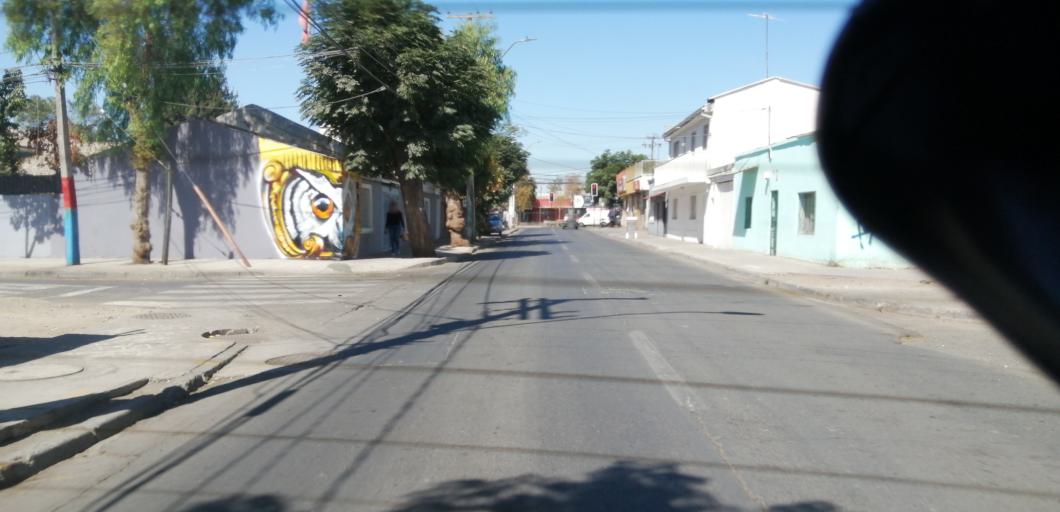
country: CL
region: Santiago Metropolitan
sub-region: Provincia de Santiago
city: Lo Prado
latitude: -33.4423
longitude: -70.7582
